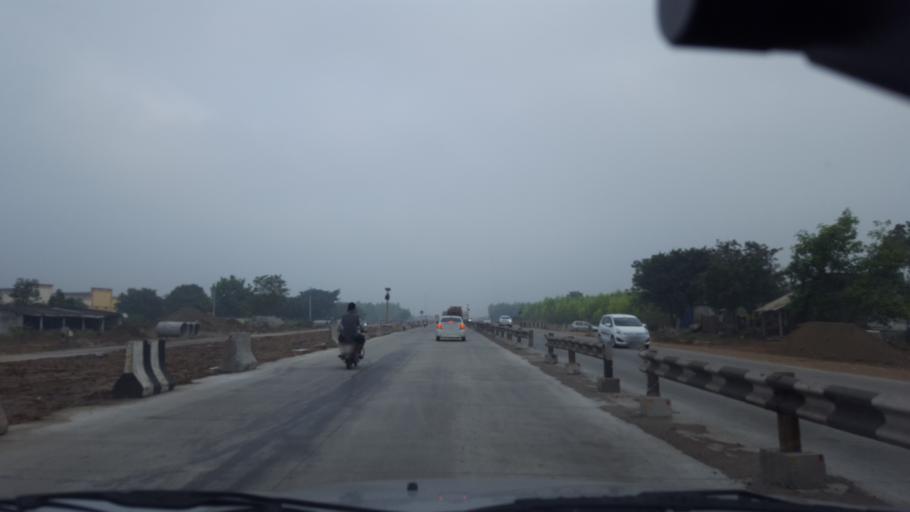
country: IN
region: Andhra Pradesh
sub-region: Prakasam
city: Addanki
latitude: 15.7924
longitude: 80.0384
